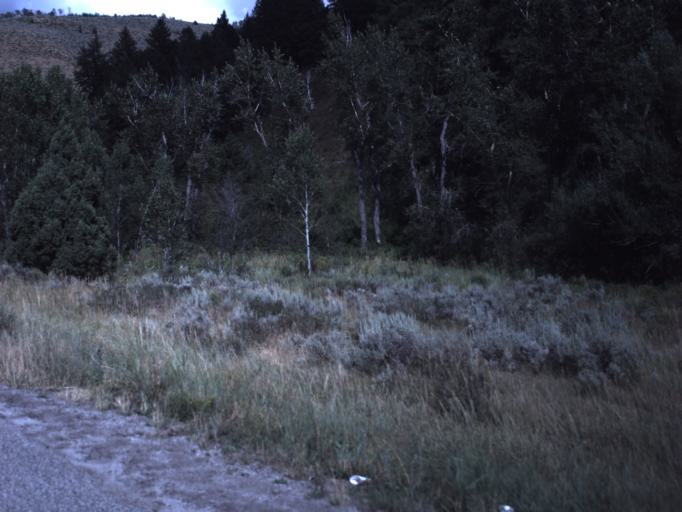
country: US
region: Utah
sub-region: Cache County
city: North Logan
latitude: 41.8461
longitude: -111.5874
